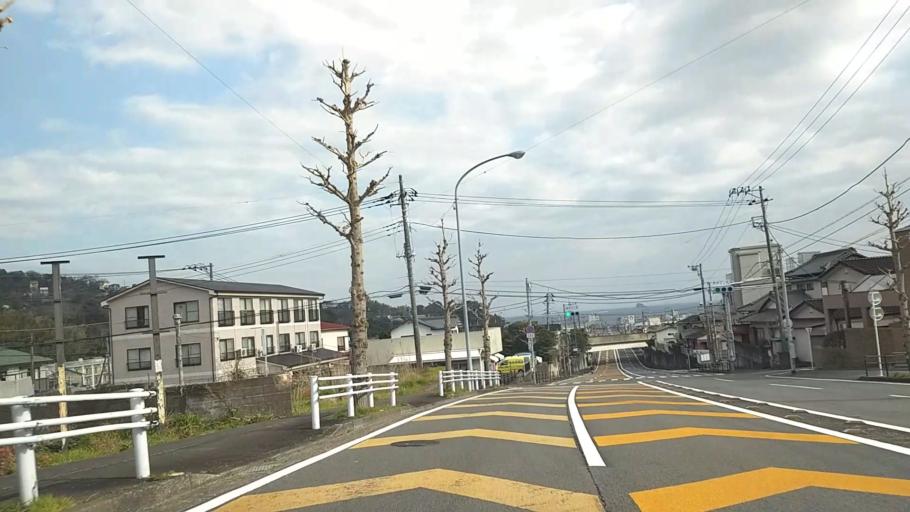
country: JP
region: Shizuoka
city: Ito
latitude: 35.0122
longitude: 139.0762
